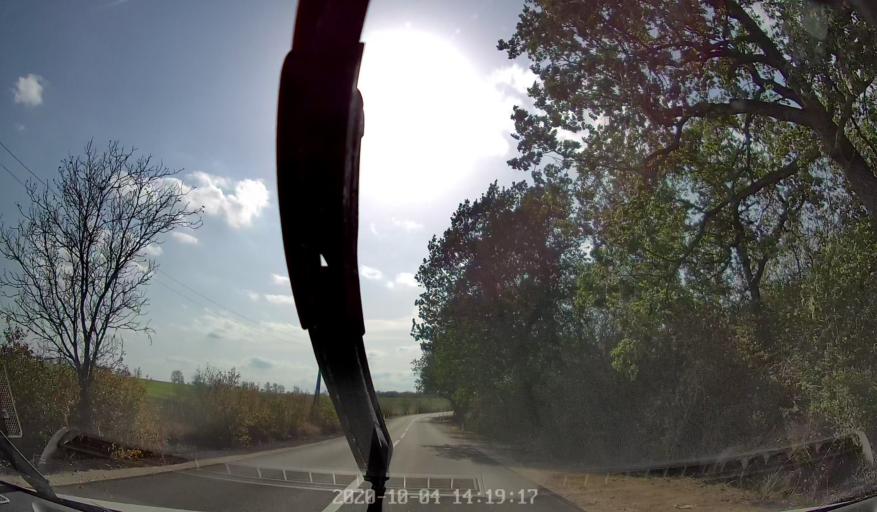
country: MD
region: Rezina
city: Saharna
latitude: 47.5922
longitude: 28.9749
